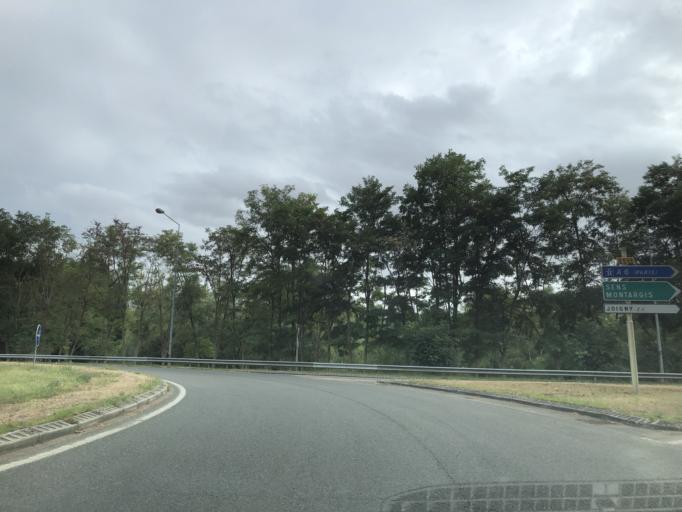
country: FR
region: Bourgogne
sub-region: Departement de l'Yonne
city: Joigny
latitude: 47.9709
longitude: 3.4094
